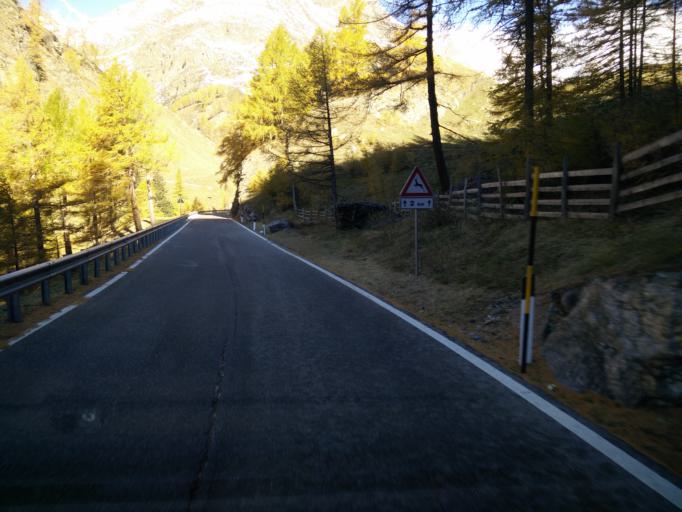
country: IT
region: Trentino-Alto Adige
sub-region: Bolzano
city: Moso in Passiria
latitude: 46.8936
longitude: 11.1309
